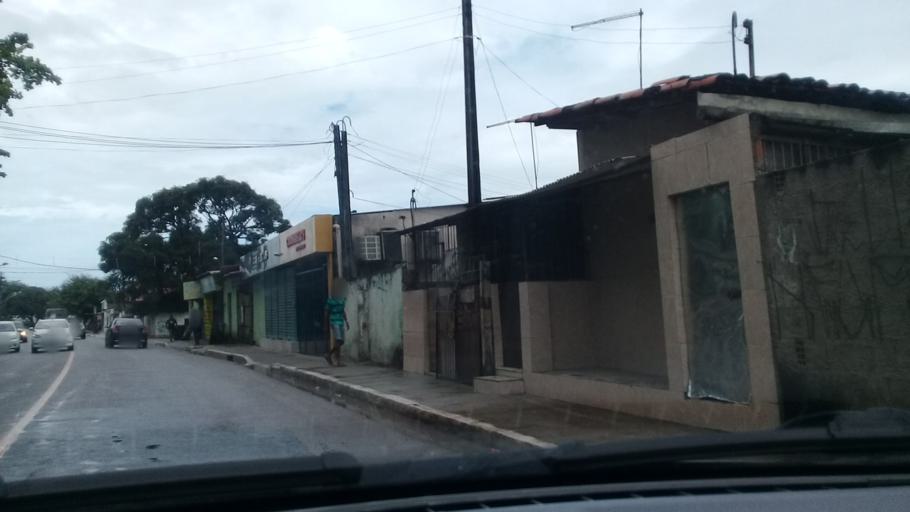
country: BR
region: Pernambuco
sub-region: Jaboatao Dos Guararapes
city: Jaboatao
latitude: -8.1405
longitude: -34.9233
